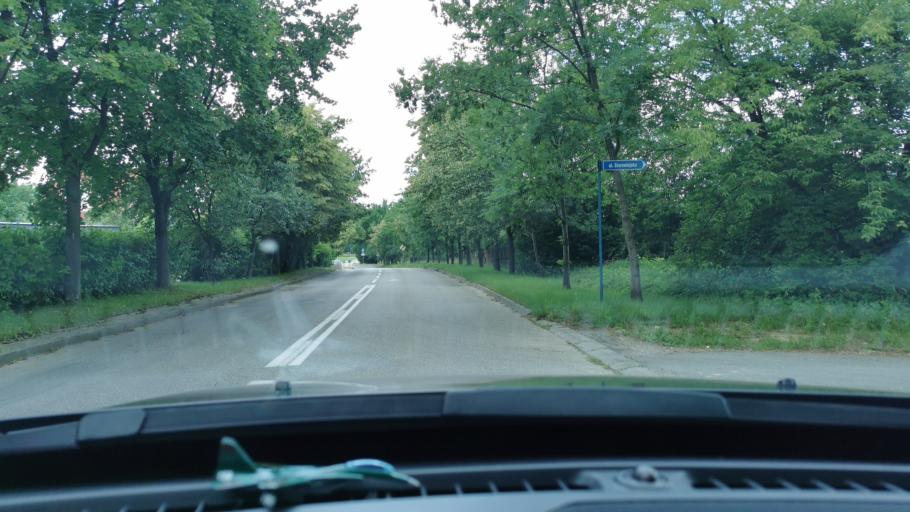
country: PL
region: Lesser Poland Voivodeship
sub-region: Powiat chrzanowski
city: Chrzanow
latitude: 50.1336
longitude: 19.4109
